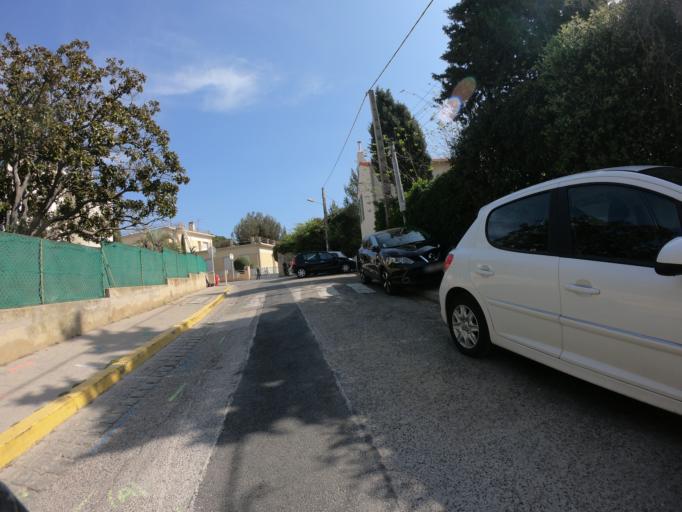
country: FR
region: Provence-Alpes-Cote d'Azur
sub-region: Departement du Var
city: Toulon
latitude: 43.1042
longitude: 5.9313
